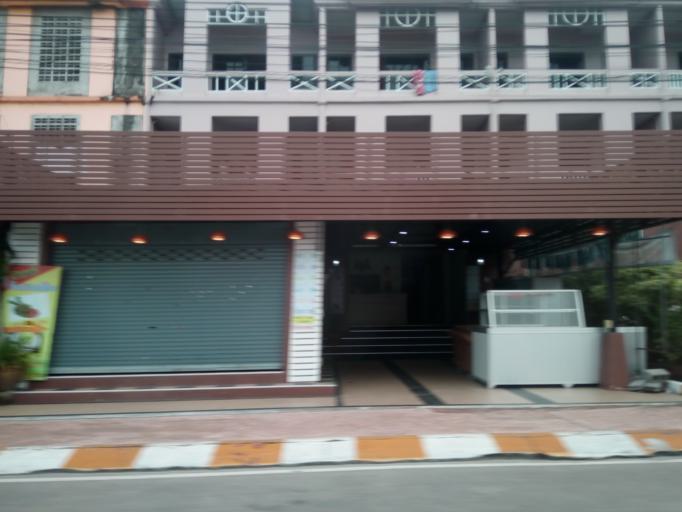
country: TH
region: Phuket
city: Mueang Phuket
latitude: 7.8813
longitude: 98.3648
